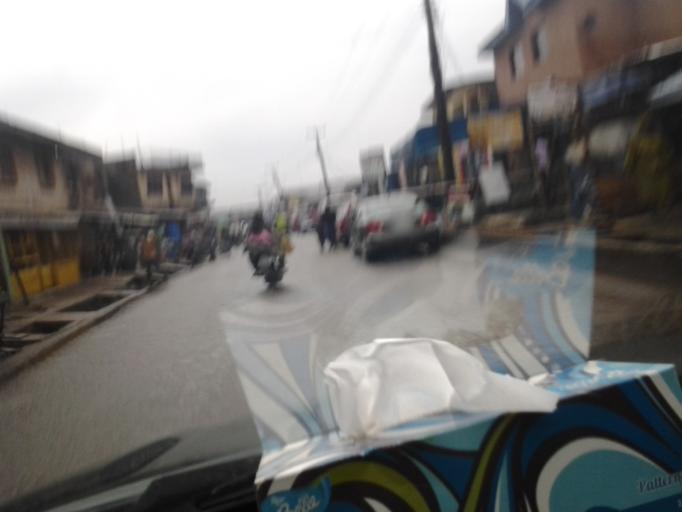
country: NG
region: Oyo
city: Ibadan
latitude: 7.4417
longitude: 3.9089
